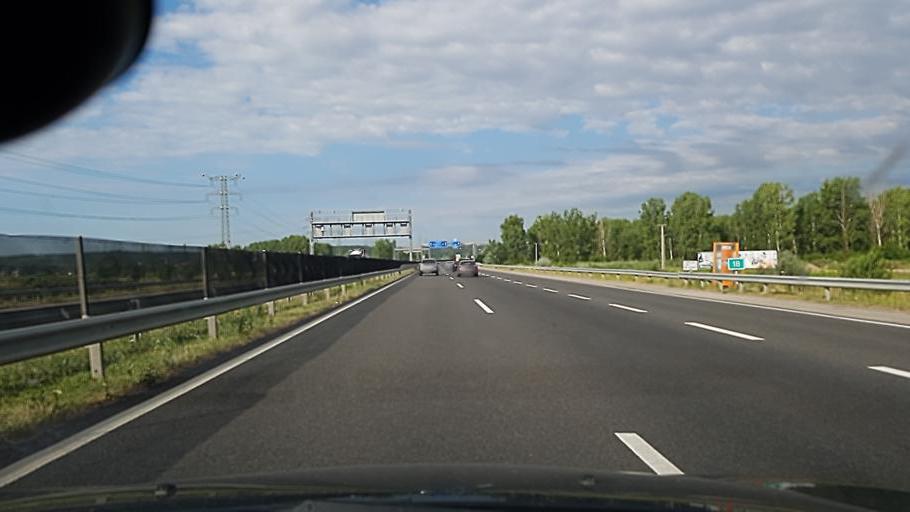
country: HU
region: Pest
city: Diosd
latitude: 47.3769
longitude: 18.9483
